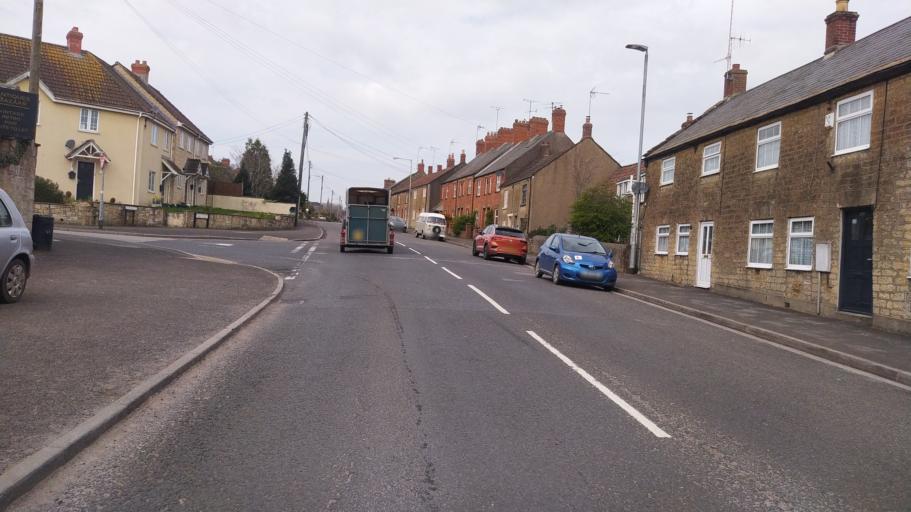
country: GB
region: England
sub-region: Somerset
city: Crewkerne
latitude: 50.8800
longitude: -2.7857
